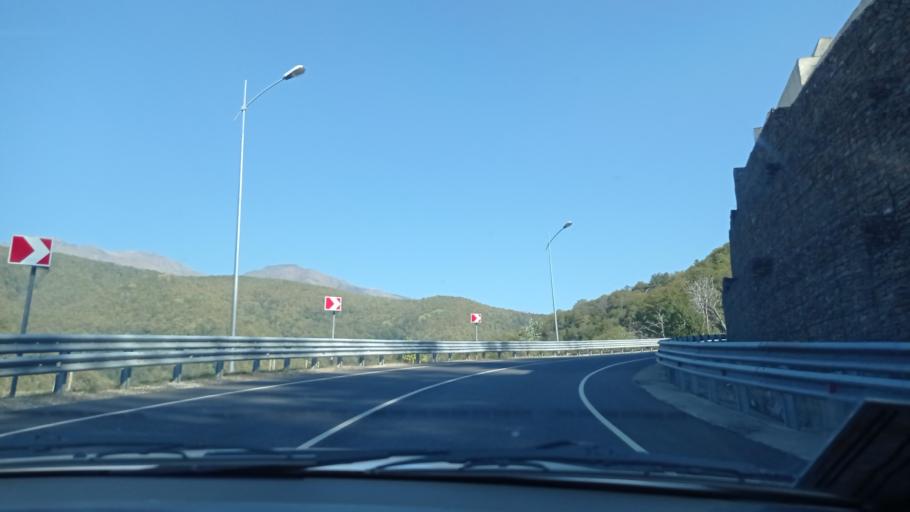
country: RU
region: Krasnodarskiy
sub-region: Sochi City
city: Krasnaya Polyana
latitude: 43.6812
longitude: 40.2429
